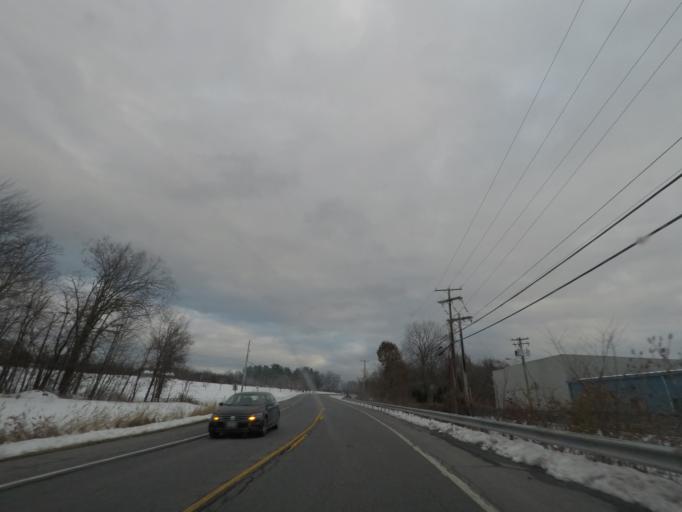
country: US
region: New York
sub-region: Ulster County
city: Plattekill
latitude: 41.6547
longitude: -74.1143
